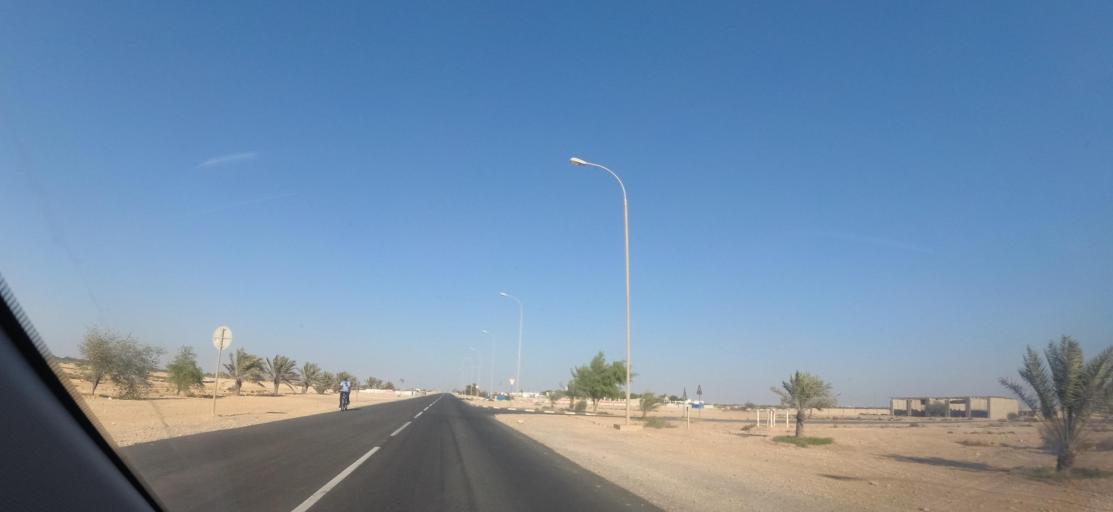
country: QA
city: Al Ghuwayriyah
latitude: 25.8341
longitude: 51.2540
